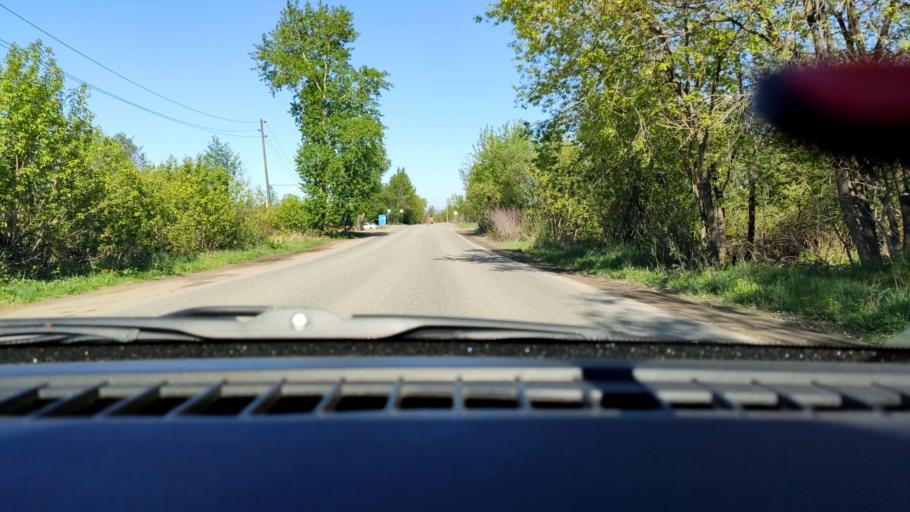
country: RU
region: Perm
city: Kondratovo
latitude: 58.0086
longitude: 56.0844
